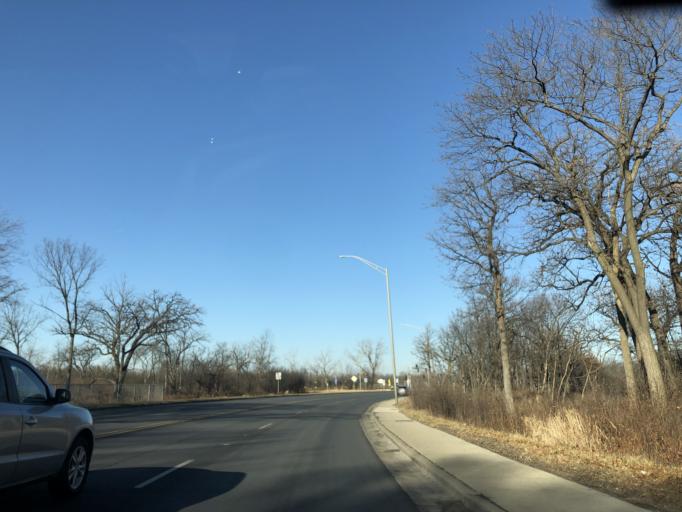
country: US
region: Illinois
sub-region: Cook County
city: Riverside
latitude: 41.8376
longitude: -87.8321
